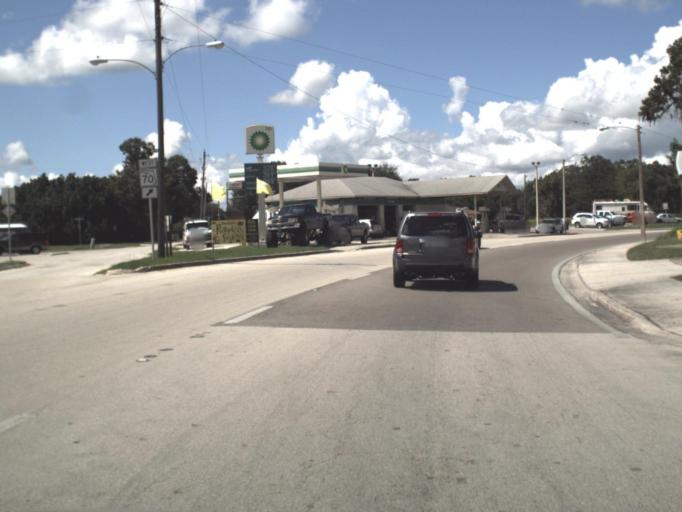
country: US
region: Florida
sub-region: DeSoto County
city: Arcadia
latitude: 27.2118
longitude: -81.8495
